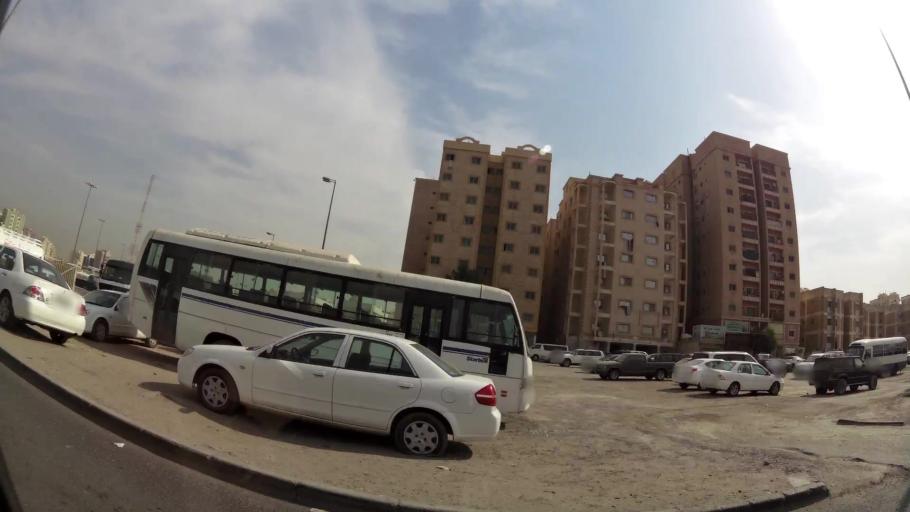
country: KW
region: Al Farwaniyah
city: Al Farwaniyah
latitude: 29.2794
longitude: 47.9686
